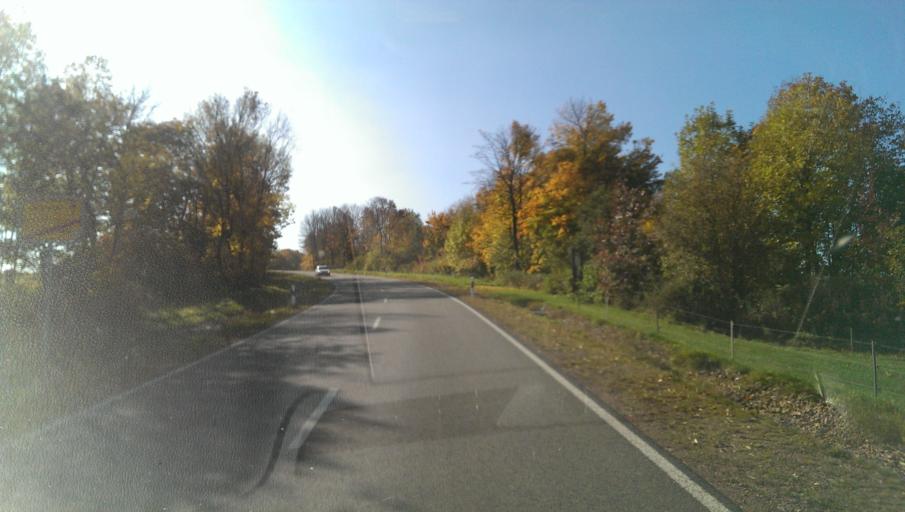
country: DE
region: Saxony
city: Barenstein
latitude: 50.7856
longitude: 13.8552
